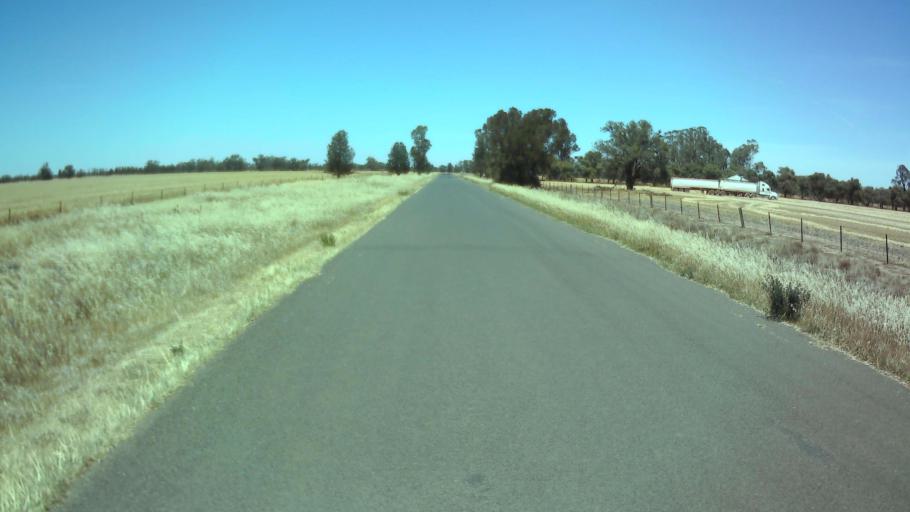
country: AU
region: New South Wales
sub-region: Weddin
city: Grenfell
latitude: -34.0296
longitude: 147.7909
